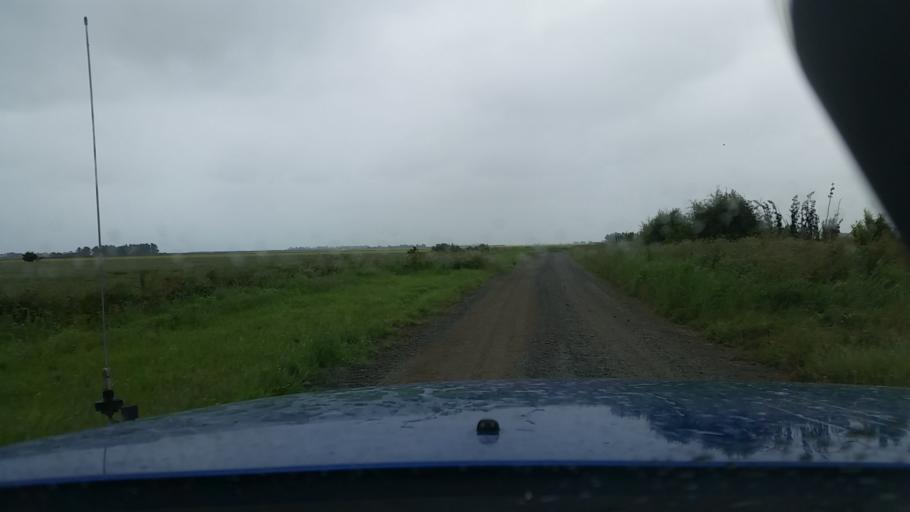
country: NZ
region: Canterbury
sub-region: Ashburton District
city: Tinwald
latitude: -44.0512
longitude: 171.7346
